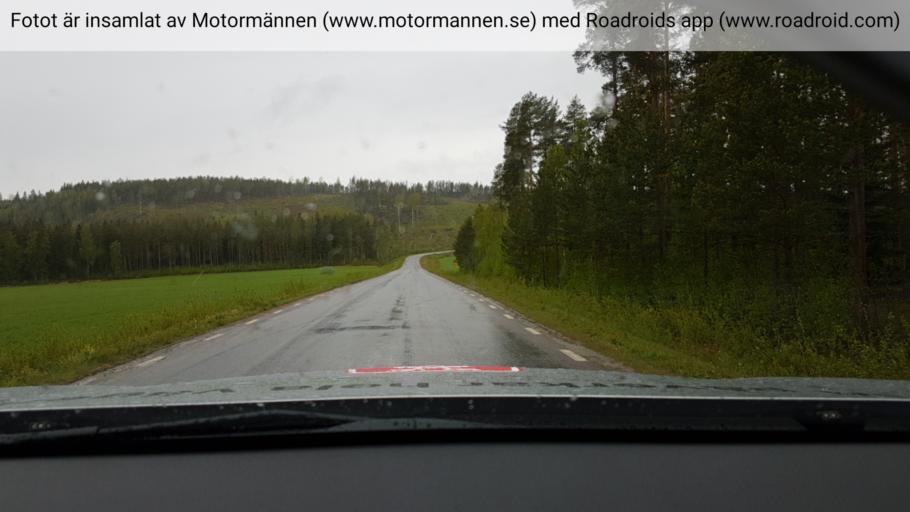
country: SE
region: Vaesterbotten
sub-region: Vannas Kommun
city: Vaennaes
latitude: 63.8908
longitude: 19.7172
